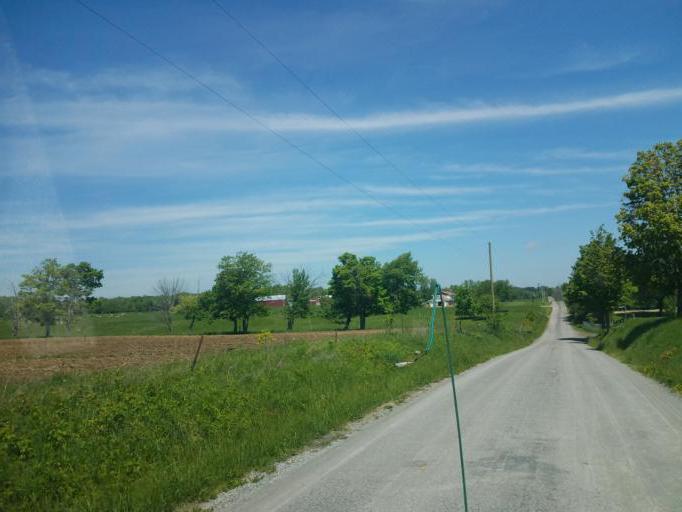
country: US
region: Ohio
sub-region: Wayne County
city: West Salem
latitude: 40.9458
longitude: -82.1790
